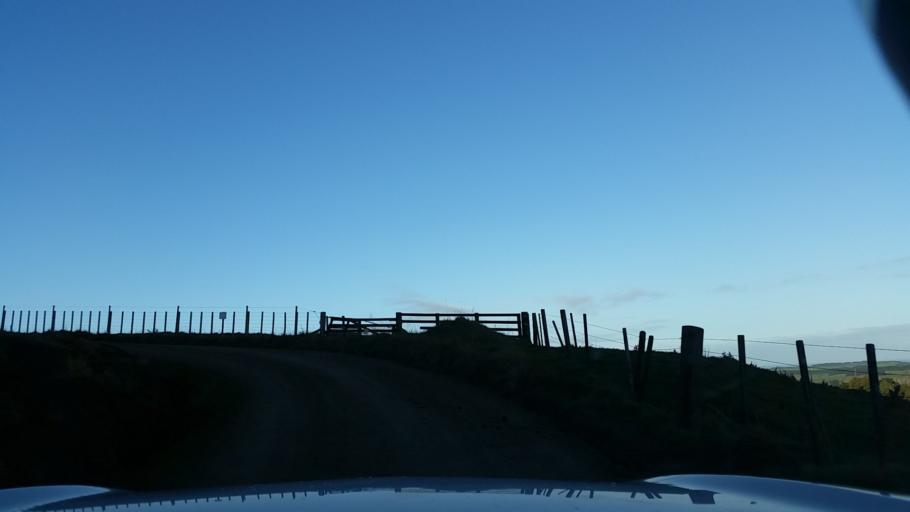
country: NZ
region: Taranaki
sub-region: South Taranaki District
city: Patea
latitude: -39.7554
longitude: 174.7470
